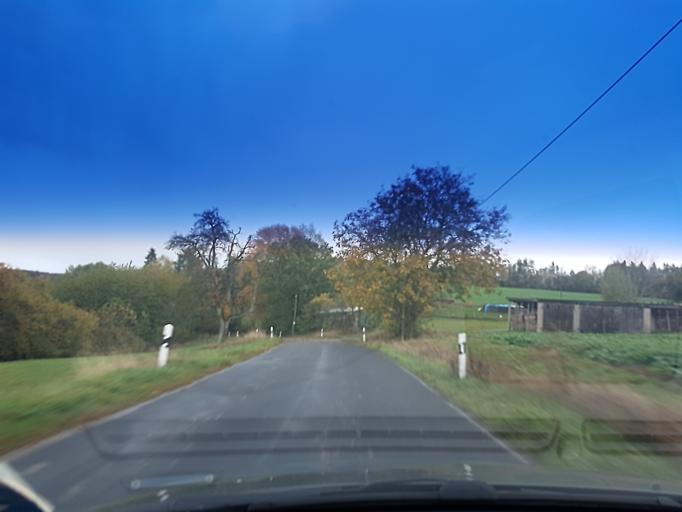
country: DE
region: Bavaria
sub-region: Regierungsbezirk Unterfranken
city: Geiselwind
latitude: 49.7576
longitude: 10.5199
